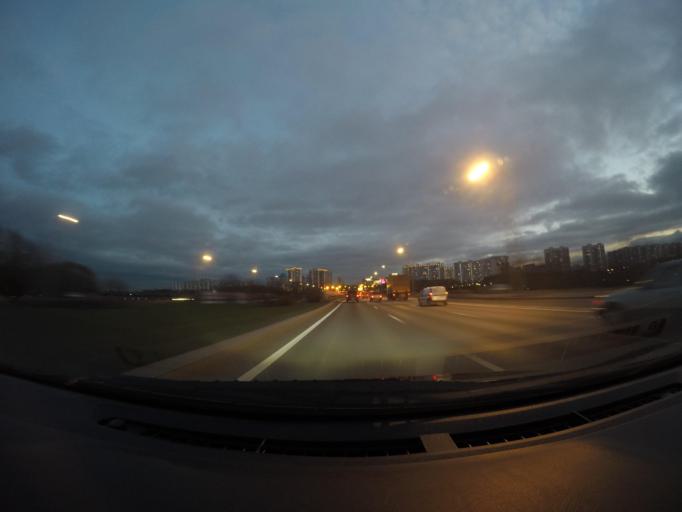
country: RU
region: Moskovskaya
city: Kur'yanovo
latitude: 55.6316
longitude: 37.7042
